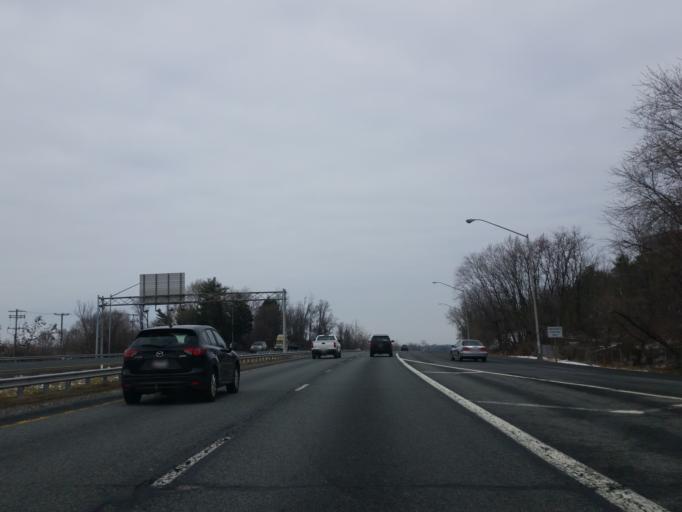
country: US
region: Maryland
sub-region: Baltimore County
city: Hunt Valley
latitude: 39.4986
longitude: -76.6676
